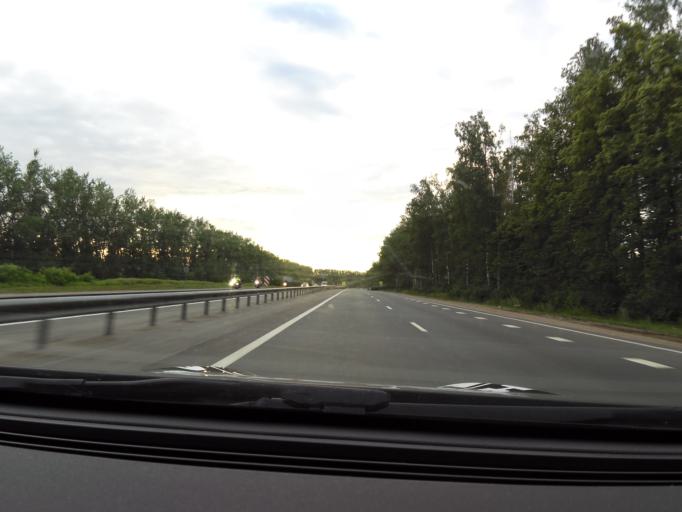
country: RU
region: Chuvashia
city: Kugesi
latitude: 56.0095
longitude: 47.3161
